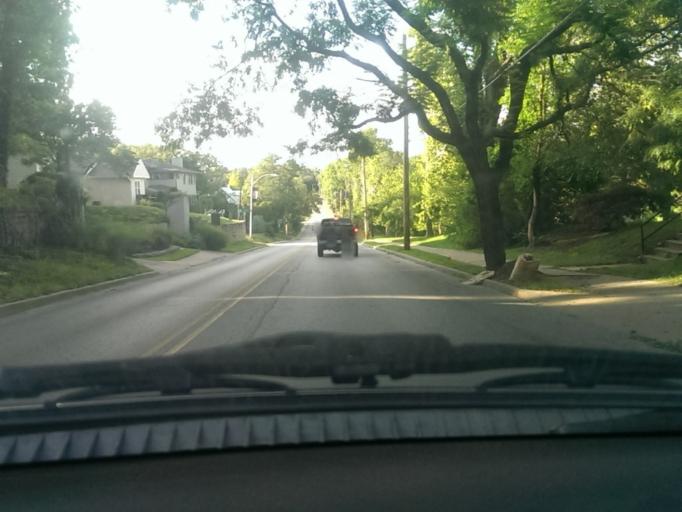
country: US
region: Kansas
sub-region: Johnson County
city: Westwood
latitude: 39.0405
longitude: -94.6074
